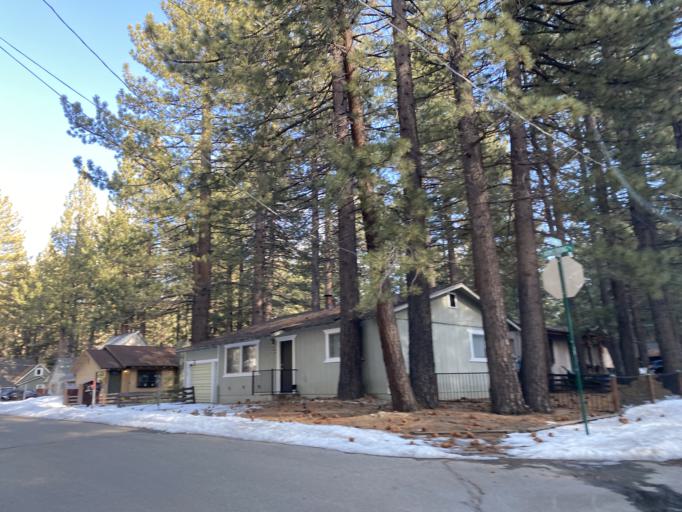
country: US
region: California
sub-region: El Dorado County
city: South Lake Tahoe
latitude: 38.9238
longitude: -119.9822
